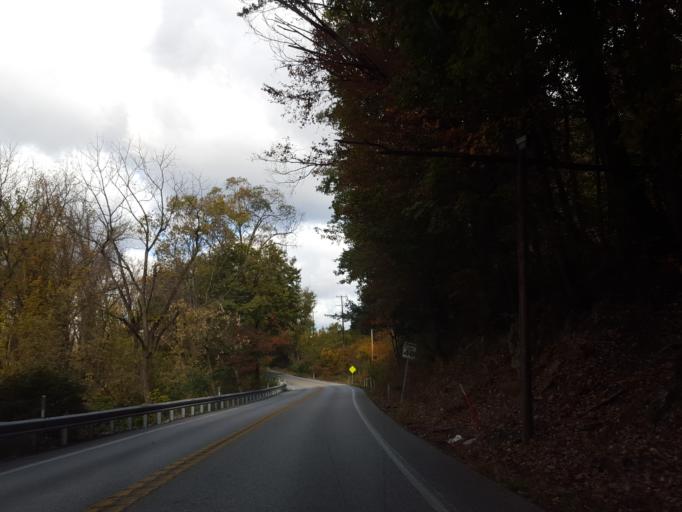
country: US
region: Pennsylvania
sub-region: York County
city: Yoe
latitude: 39.9265
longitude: -76.6494
